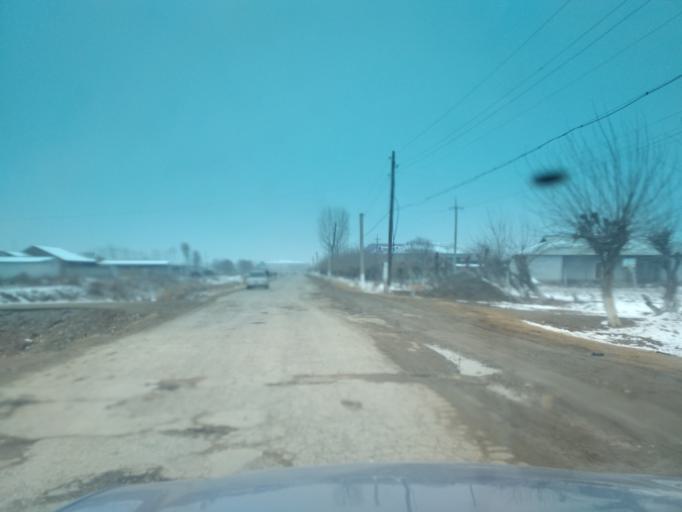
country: UZ
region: Sirdaryo
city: Guliston
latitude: 40.4811
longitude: 68.7513
